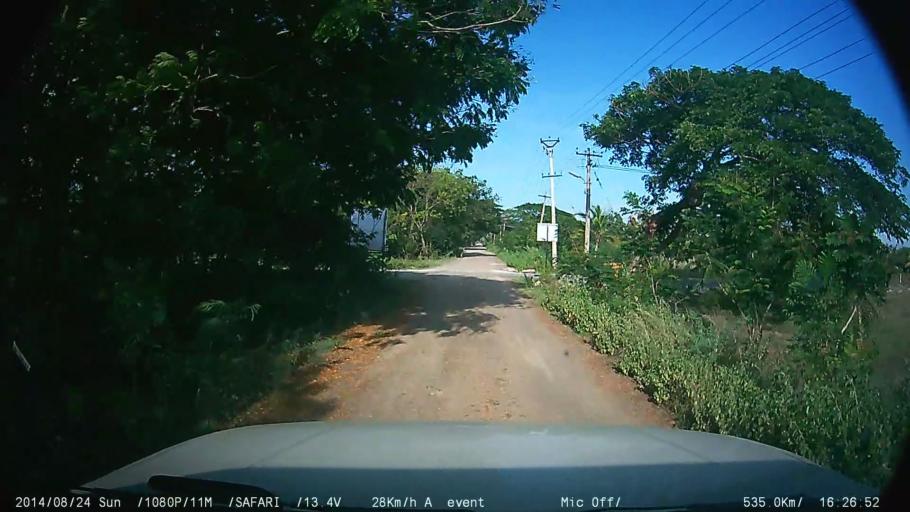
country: IN
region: Tamil Nadu
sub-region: Kancheepuram
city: Vengavasal
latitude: 12.8162
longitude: 80.2182
